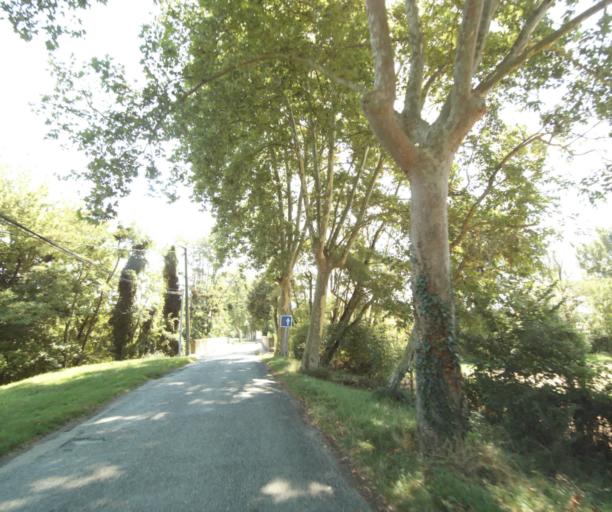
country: FR
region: Midi-Pyrenees
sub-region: Departement de l'Ariege
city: Lezat-sur-Leze
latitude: 43.2746
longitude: 1.3534
